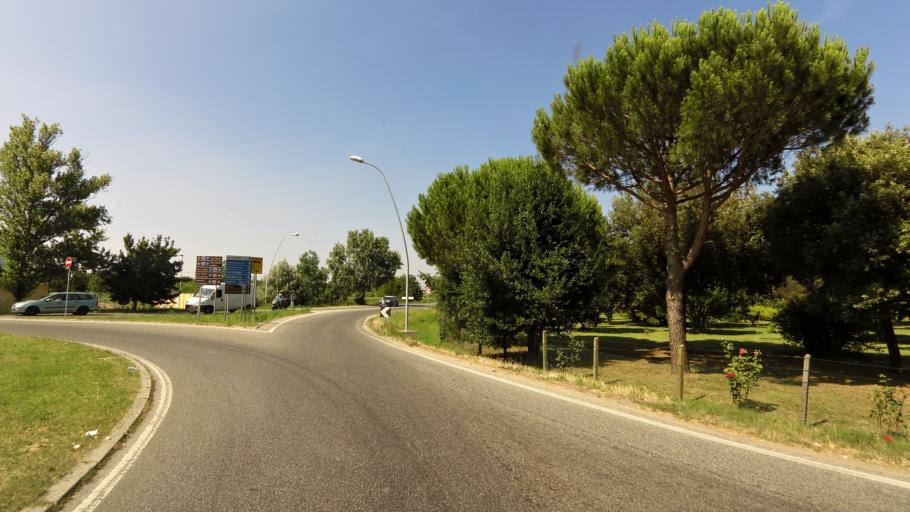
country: IT
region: Emilia-Romagna
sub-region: Provincia di Ravenna
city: Porto Fuori
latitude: 44.4101
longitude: 12.2305
